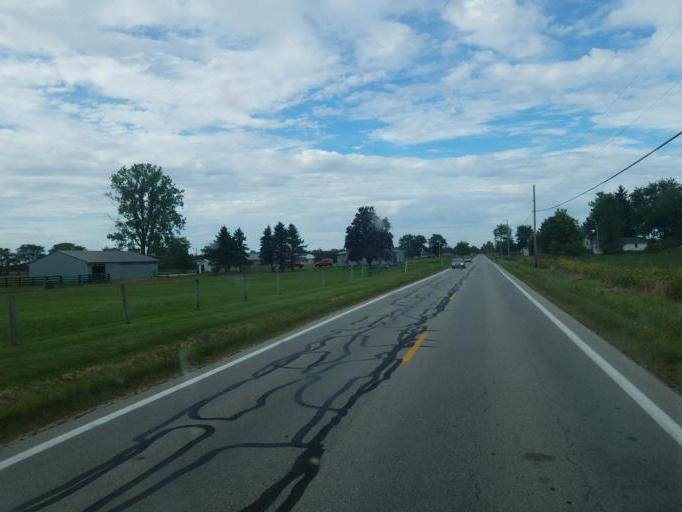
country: US
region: Ohio
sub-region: Delaware County
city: Sunbury
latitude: 40.1929
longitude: -82.8054
